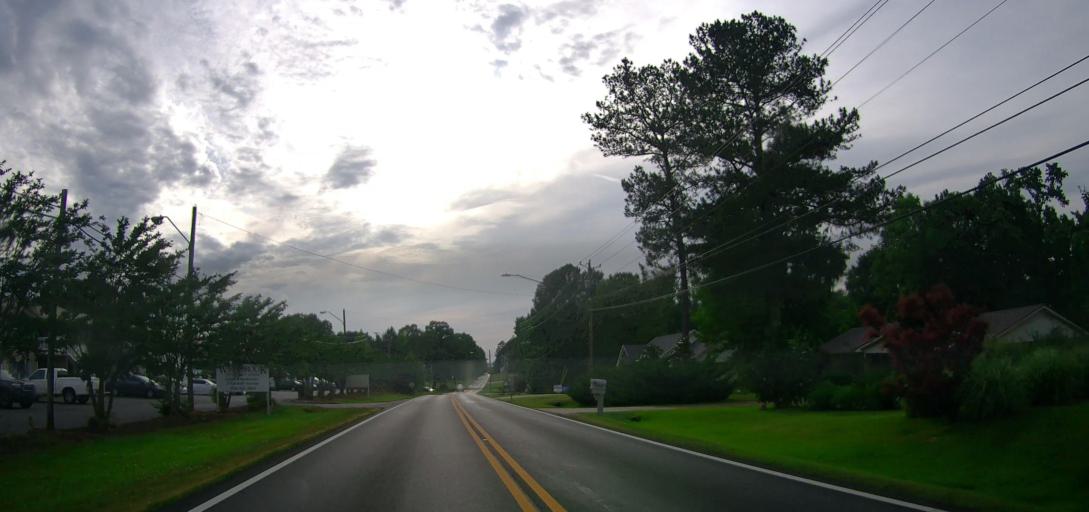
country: US
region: Alabama
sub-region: Calhoun County
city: Oxford
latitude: 33.5857
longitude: -85.7993
